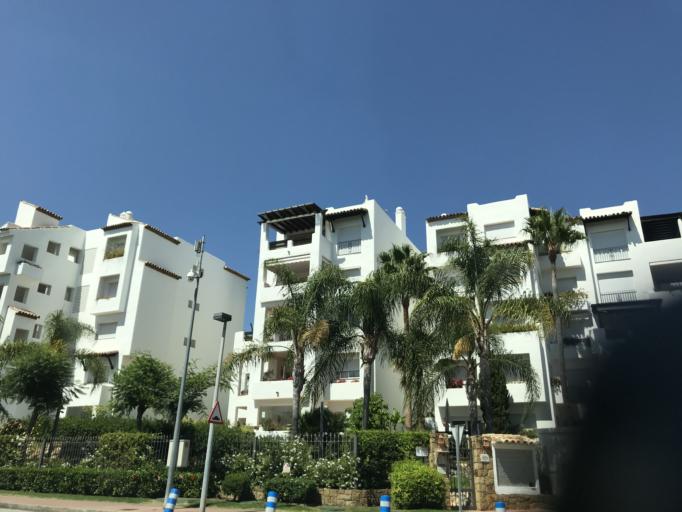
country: ES
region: Andalusia
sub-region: Provincia de Malaga
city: Benahavis
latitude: 36.4584
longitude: -5.0471
